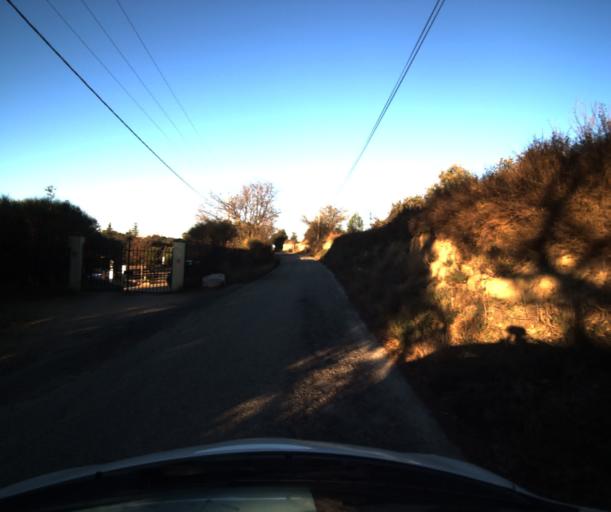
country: FR
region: Provence-Alpes-Cote d'Azur
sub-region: Departement du Vaucluse
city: Pertuis
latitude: 43.7033
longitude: 5.4732
